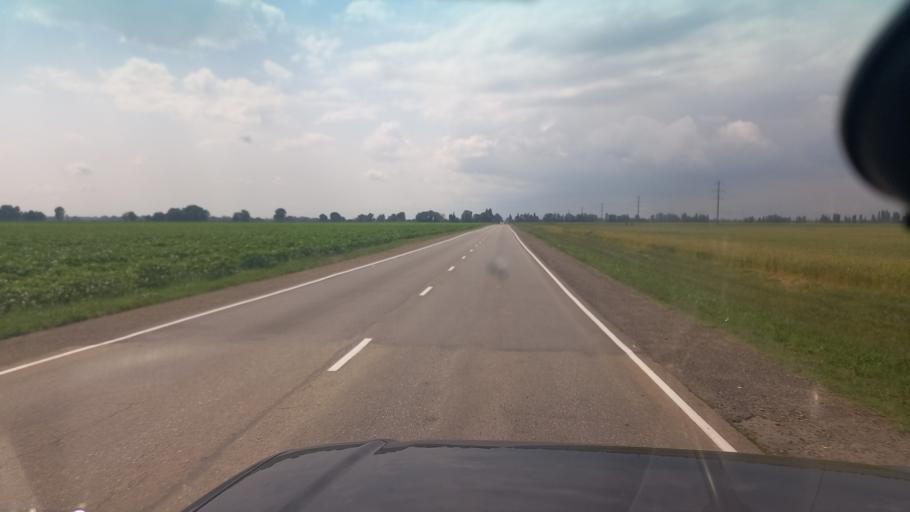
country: RU
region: Adygeya
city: Koshekhabl'
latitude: 44.9065
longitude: 40.4621
